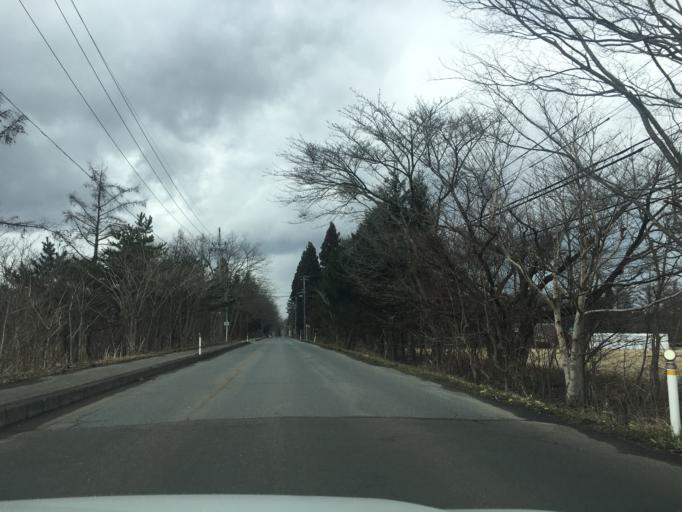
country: JP
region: Akita
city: Takanosu
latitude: 40.1798
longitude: 140.3454
